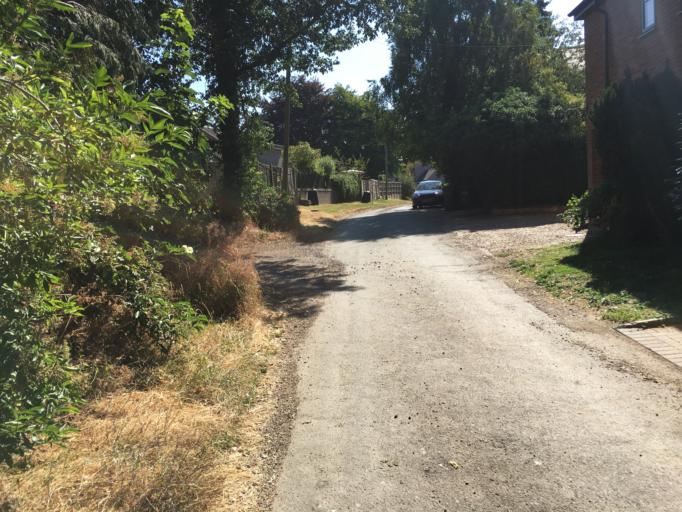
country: GB
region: England
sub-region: Warwickshire
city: Rugby
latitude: 52.3978
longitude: -1.2232
